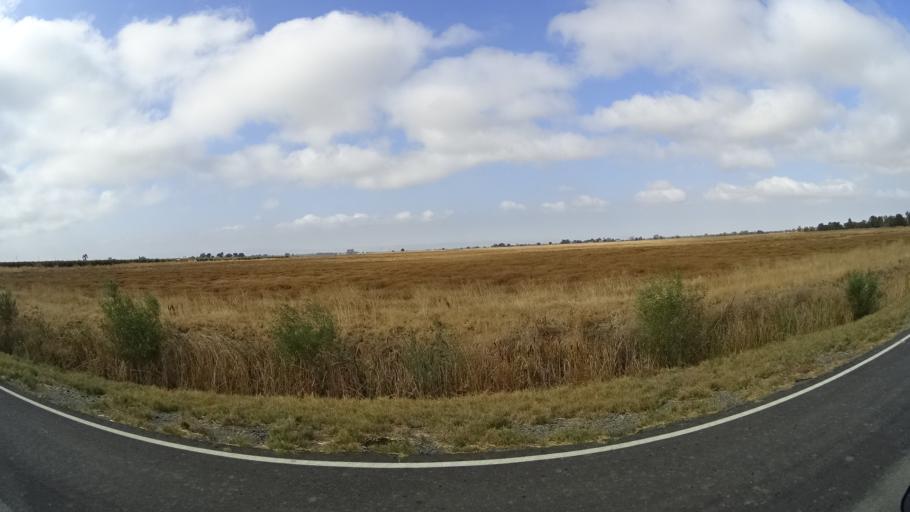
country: US
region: California
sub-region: Yolo County
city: Woodland
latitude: 38.8014
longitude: -121.7744
